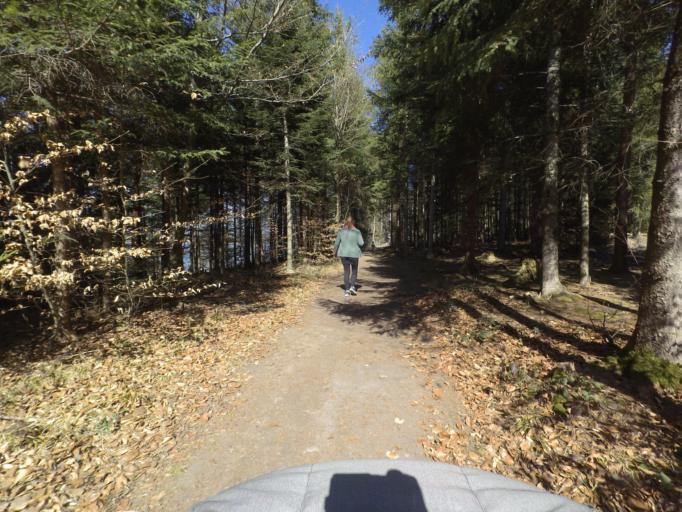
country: AT
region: Salzburg
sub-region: Politischer Bezirk Salzburg-Umgebung
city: Mattsee
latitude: 47.9912
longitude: 13.1014
